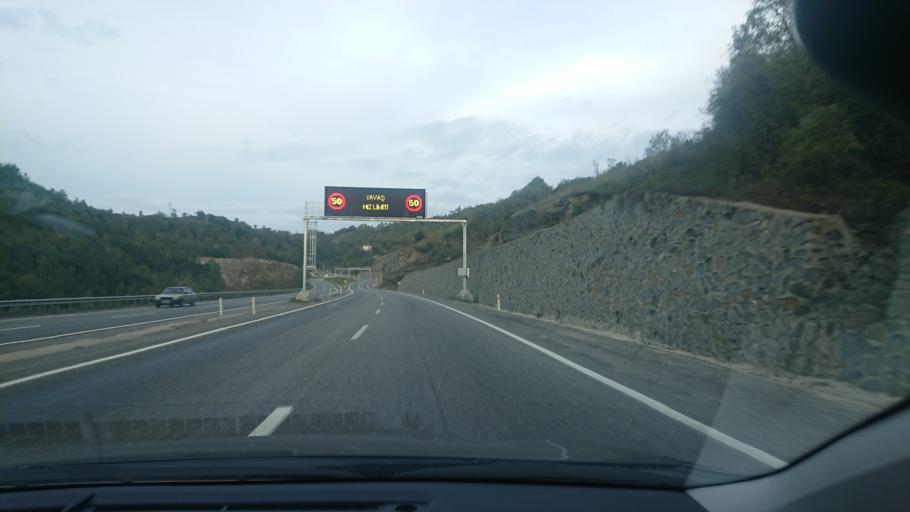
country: TR
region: Zonguldak
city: Beycuma
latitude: 41.4096
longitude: 31.9301
